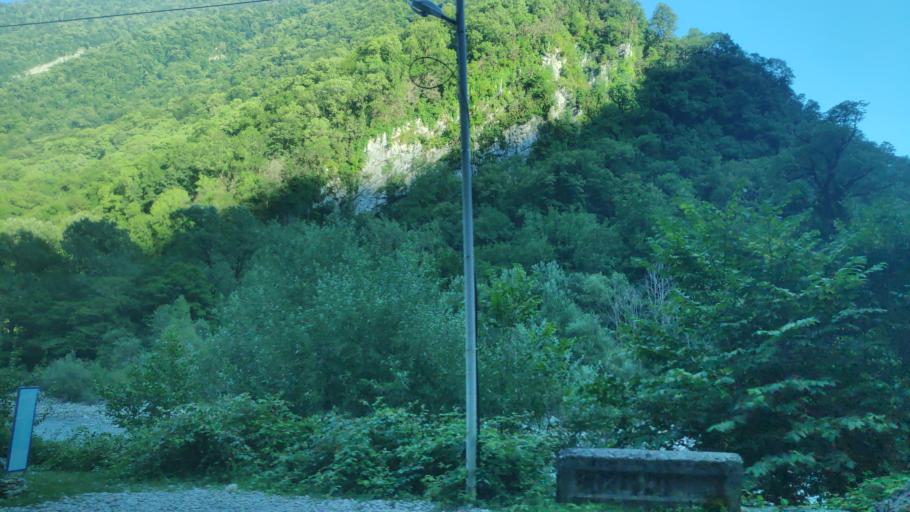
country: GE
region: Abkhazia
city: Gagra
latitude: 43.3520
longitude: 40.4140
